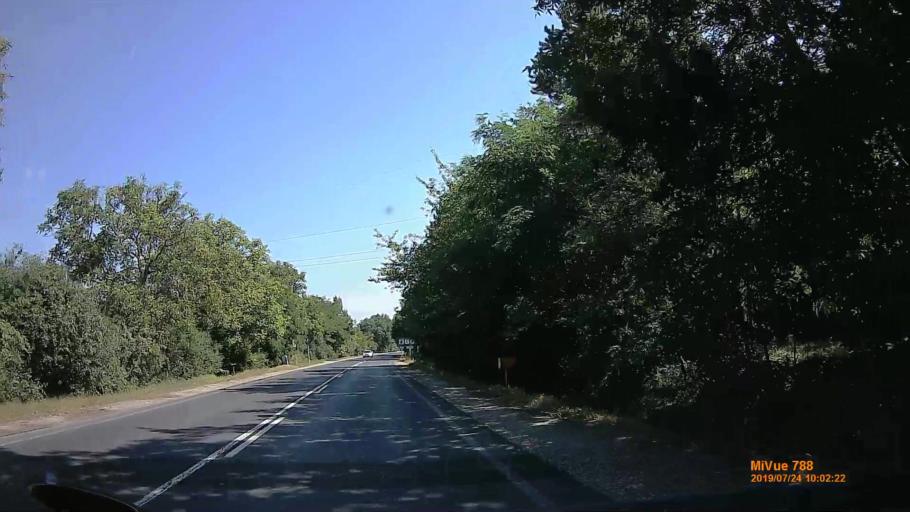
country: HU
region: Szabolcs-Szatmar-Bereg
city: Vasarosnameny
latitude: 48.1110
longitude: 22.3066
